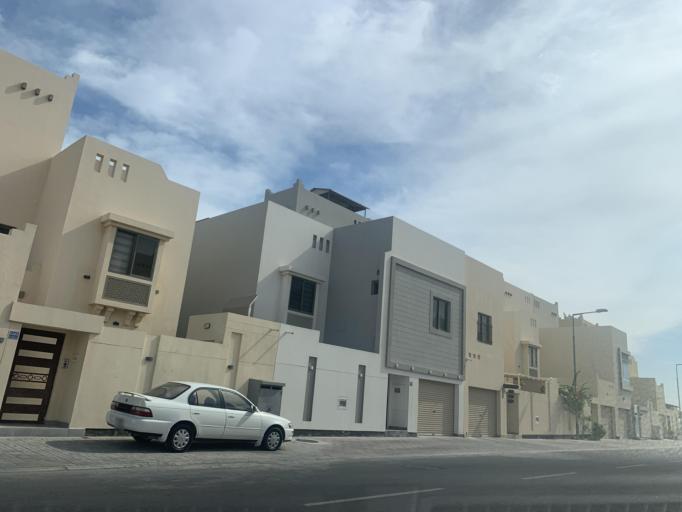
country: BH
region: Central Governorate
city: Madinat Hamad
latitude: 26.1129
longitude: 50.4893
